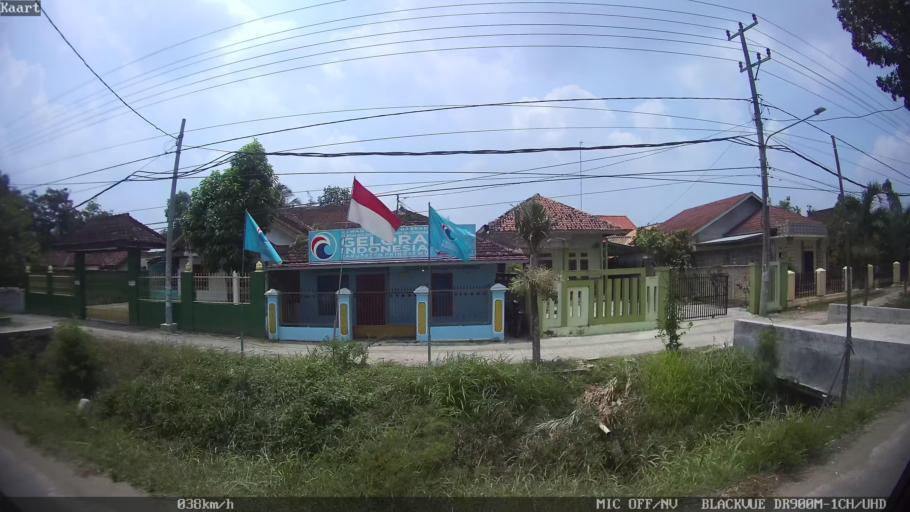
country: ID
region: Lampung
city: Pringsewu
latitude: -5.3549
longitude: 104.9672
